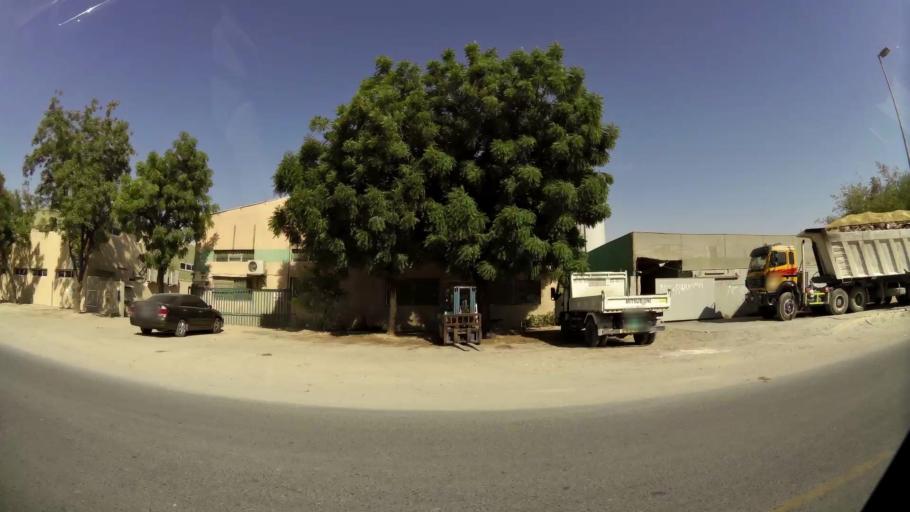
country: AE
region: Dubai
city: Dubai
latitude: 25.1280
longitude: 55.2251
